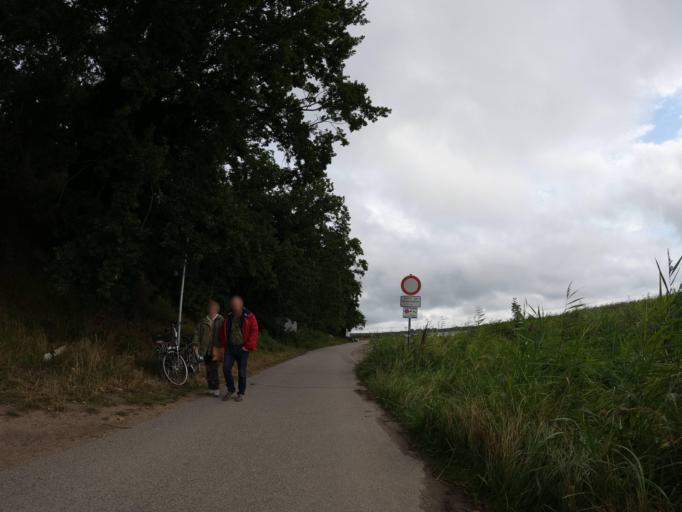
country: DE
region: Mecklenburg-Vorpommern
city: Ostseebad Gohren
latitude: 54.2827
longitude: 13.6948
